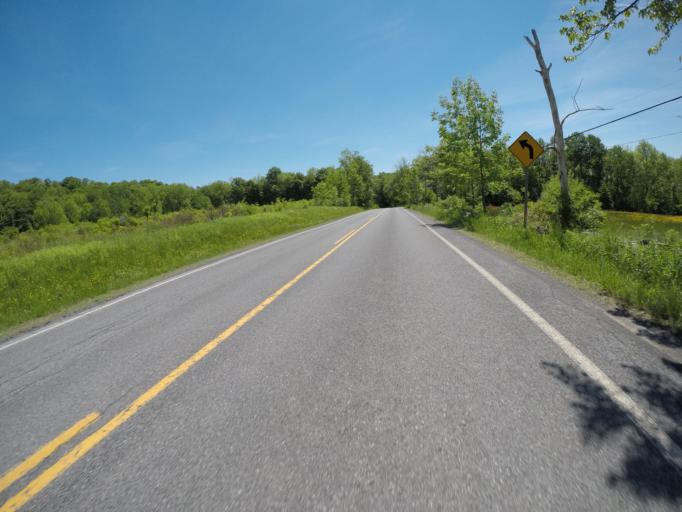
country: US
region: New York
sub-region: Delaware County
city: Delhi
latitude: 42.1964
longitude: -74.8372
